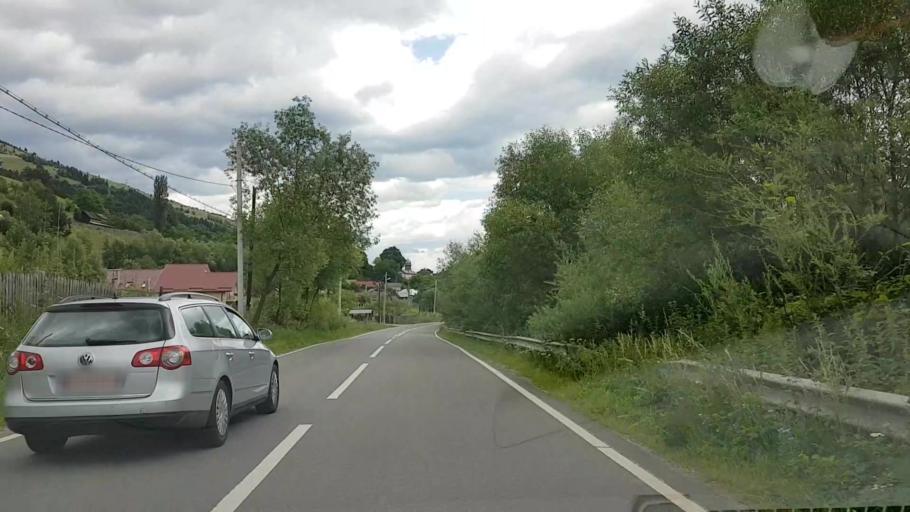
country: RO
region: Neamt
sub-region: Comuna Farcasa
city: Farcasa
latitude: 47.1695
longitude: 25.8007
